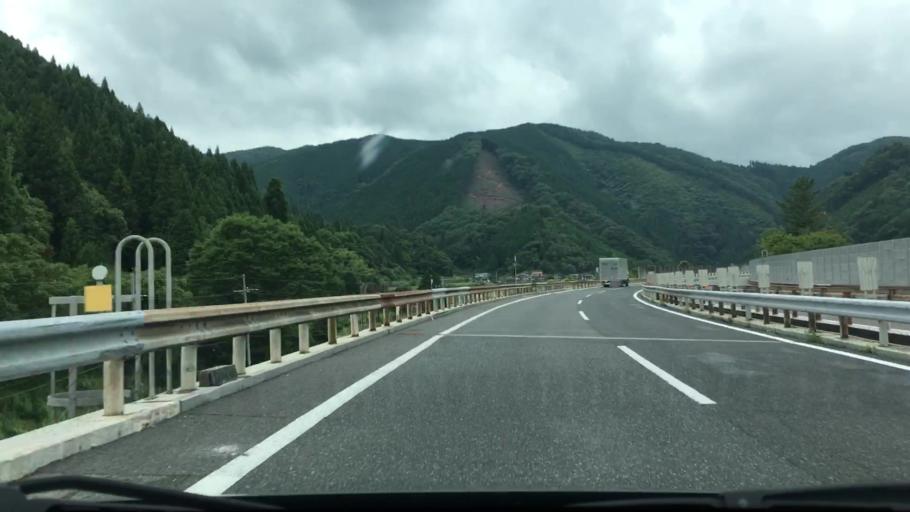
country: JP
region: Okayama
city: Niimi
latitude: 34.9749
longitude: 133.3717
